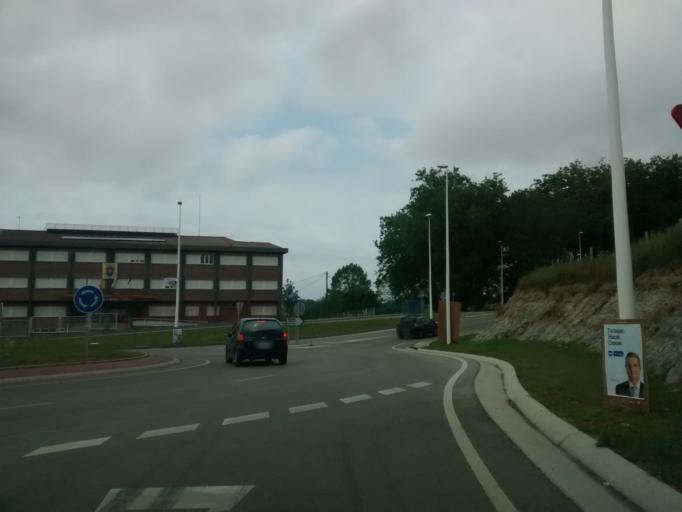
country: ES
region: Cantabria
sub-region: Provincia de Cantabria
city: Santander
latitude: 43.4218
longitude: -3.7551
